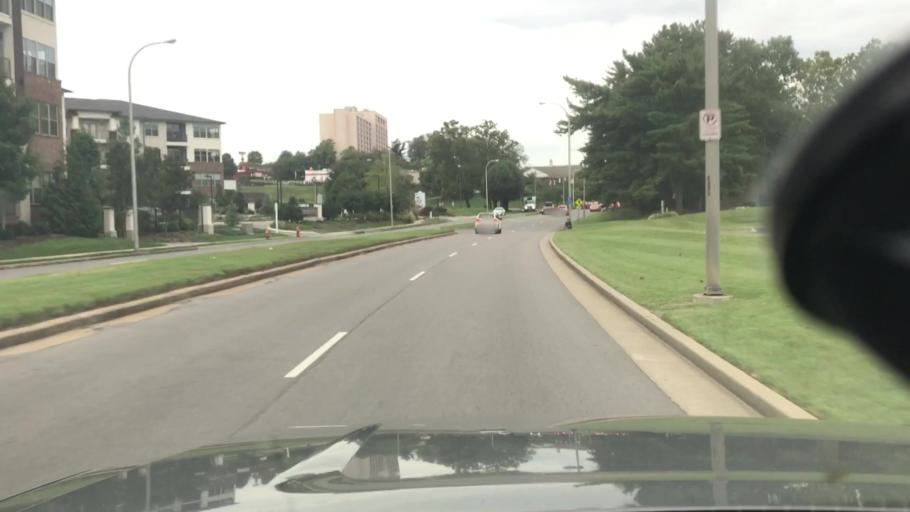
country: US
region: Tennessee
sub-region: Davidson County
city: Nashville
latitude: 36.1915
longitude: -86.7948
